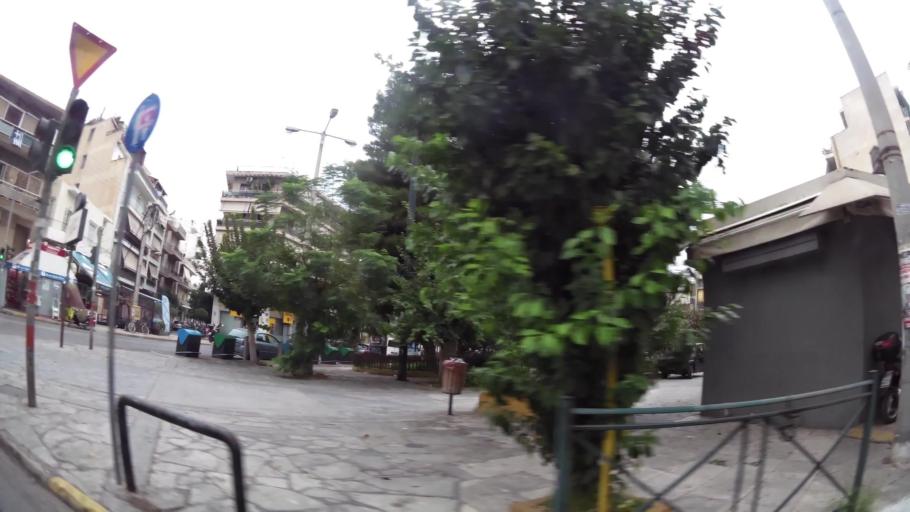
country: GR
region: Attica
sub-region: Nomos Piraios
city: Nikaia
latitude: 37.9527
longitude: 23.6559
